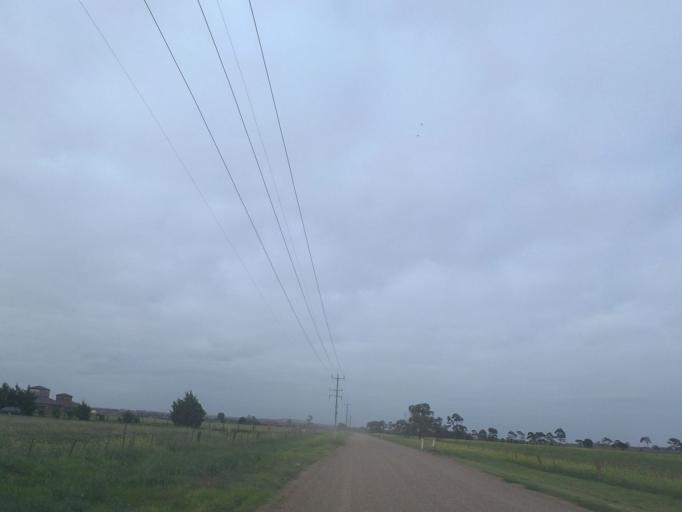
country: AU
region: Victoria
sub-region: Melton
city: Kurunjang
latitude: -37.6860
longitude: 144.6238
